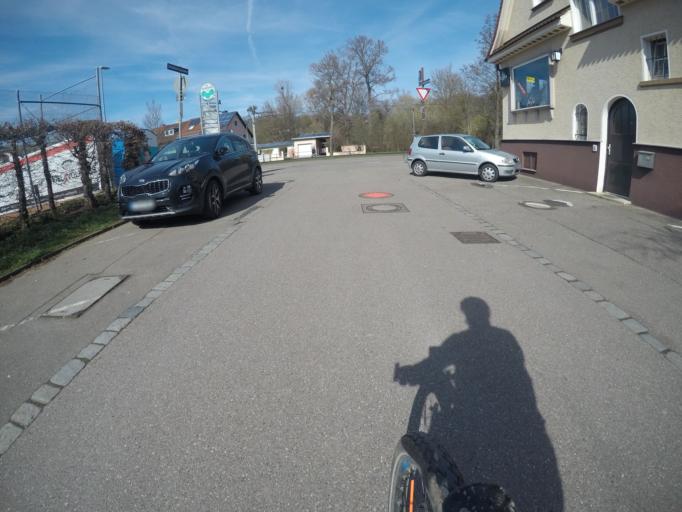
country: DE
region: Baden-Wuerttemberg
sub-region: Regierungsbezirk Stuttgart
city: Korntal
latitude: 48.8142
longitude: 9.1272
